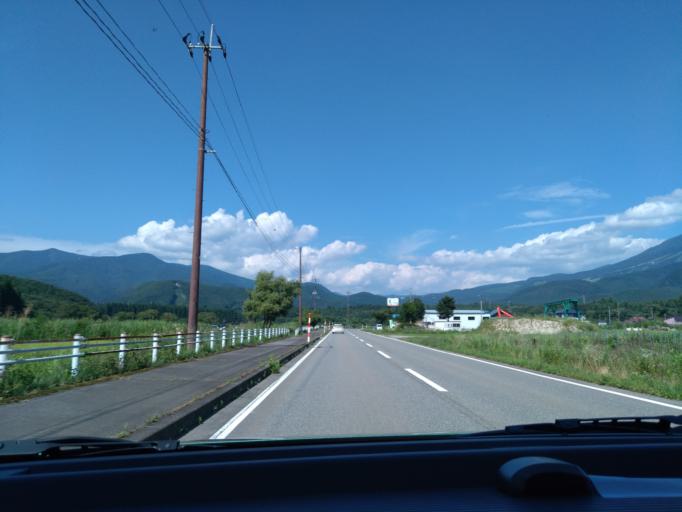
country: JP
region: Akita
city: Kakunodatemachi
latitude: 39.7390
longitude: 140.7108
